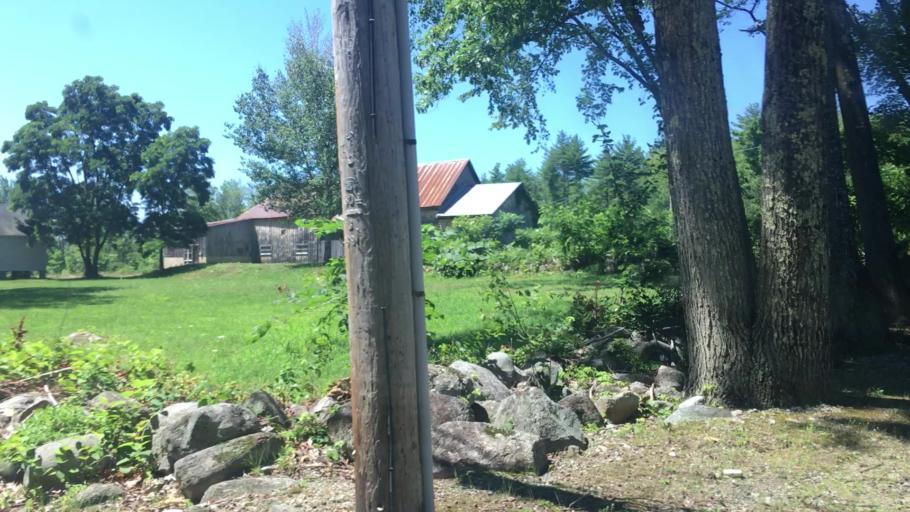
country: US
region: New Hampshire
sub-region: Merrimack County
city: Henniker
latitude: 43.1899
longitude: -71.7862
